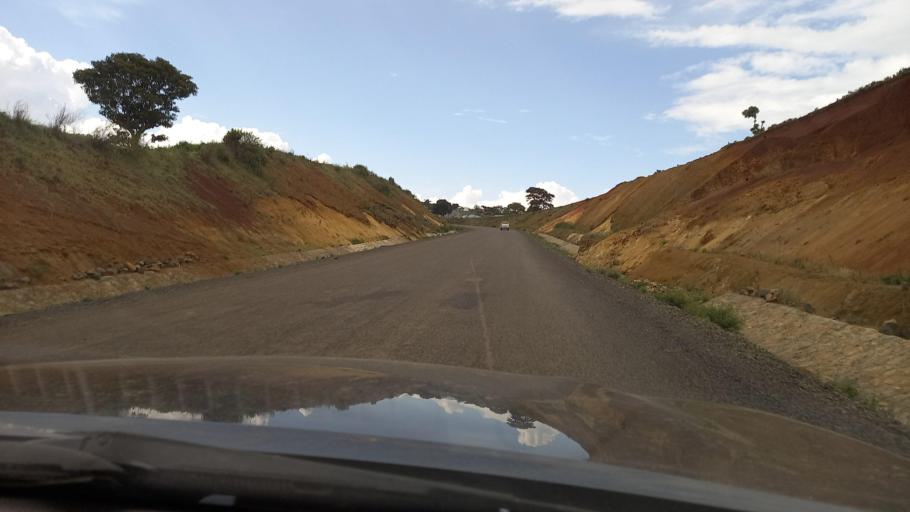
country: ET
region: Southern Nations, Nationalities, and People's Region
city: Mizan Teferi
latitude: 6.2119
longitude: 35.6418
